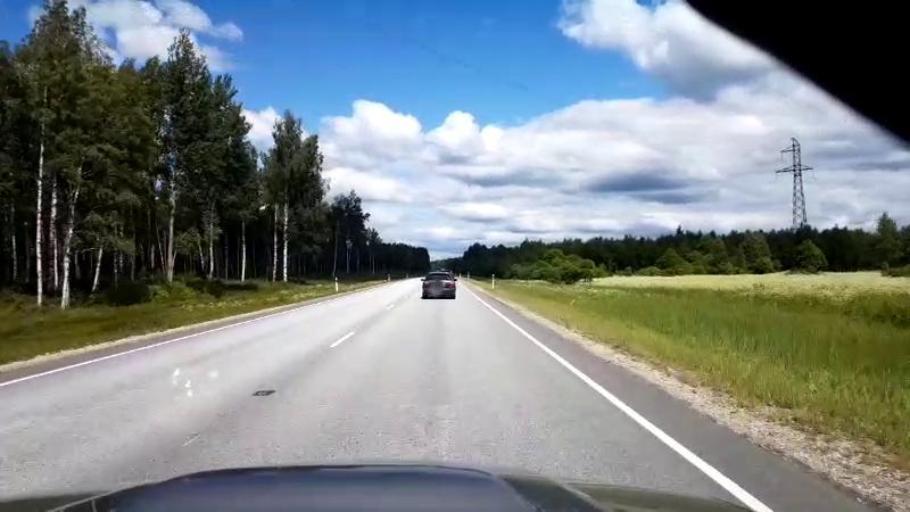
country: EE
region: Paernumaa
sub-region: Sauga vald
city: Sauga
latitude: 58.4642
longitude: 24.5188
